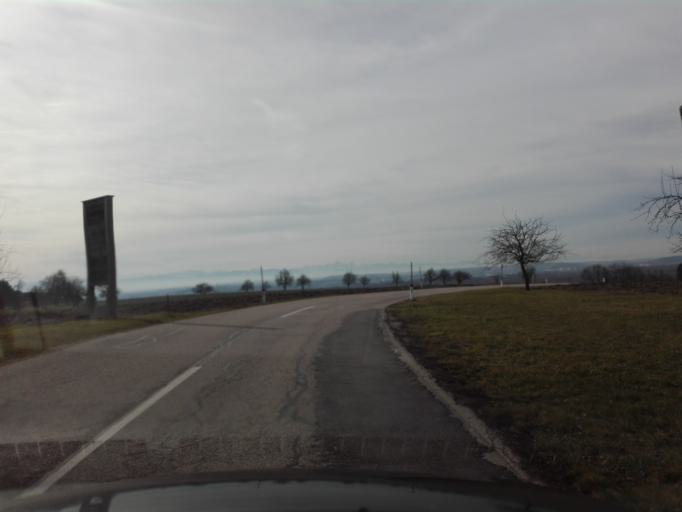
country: AT
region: Lower Austria
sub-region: Politischer Bezirk Amstetten
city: Ennsdorf
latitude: 48.2544
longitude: 14.4971
